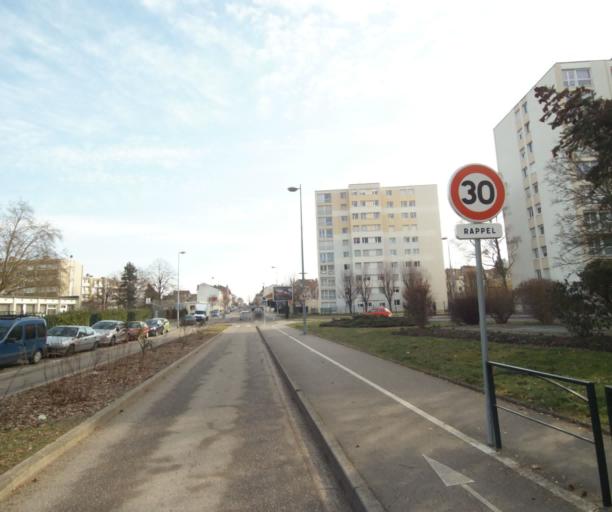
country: FR
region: Lorraine
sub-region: Departement de Meurthe-et-Moselle
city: Laxou
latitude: 48.6803
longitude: 6.1538
